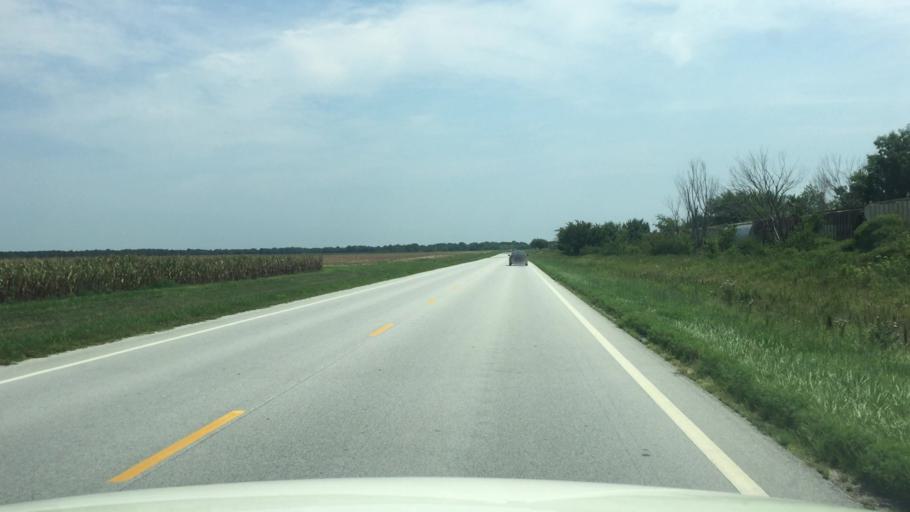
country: US
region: Kansas
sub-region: Labette County
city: Oswego
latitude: 37.1675
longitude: -95.0287
